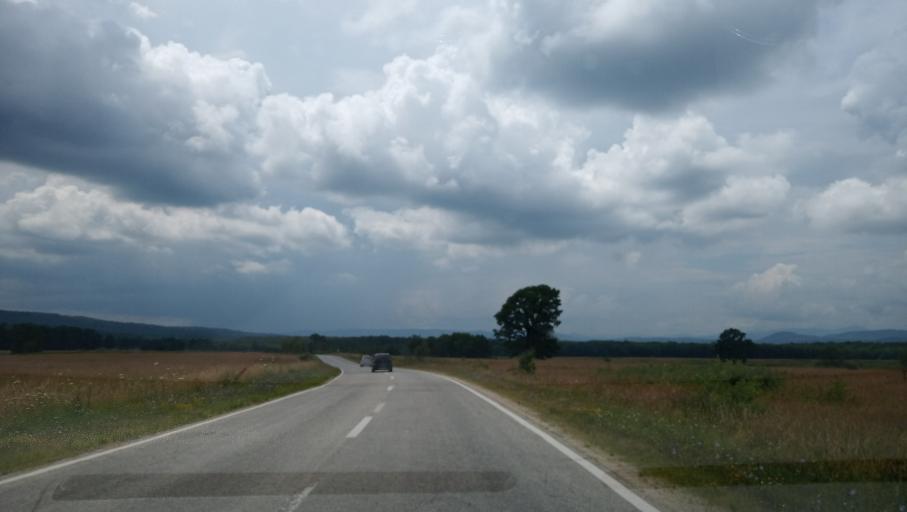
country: RO
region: Gorj
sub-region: Comuna Pestisani
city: Pestisani
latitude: 45.0625
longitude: 23.0171
